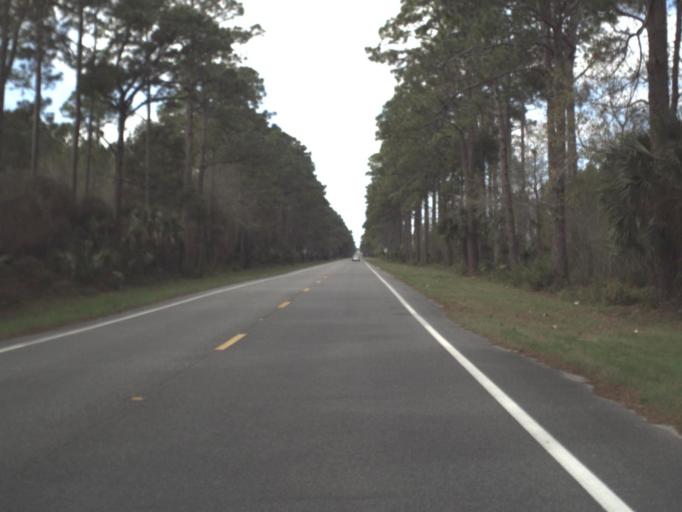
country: US
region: Florida
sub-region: Franklin County
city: Apalachicola
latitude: 29.7153
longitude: -85.0311
